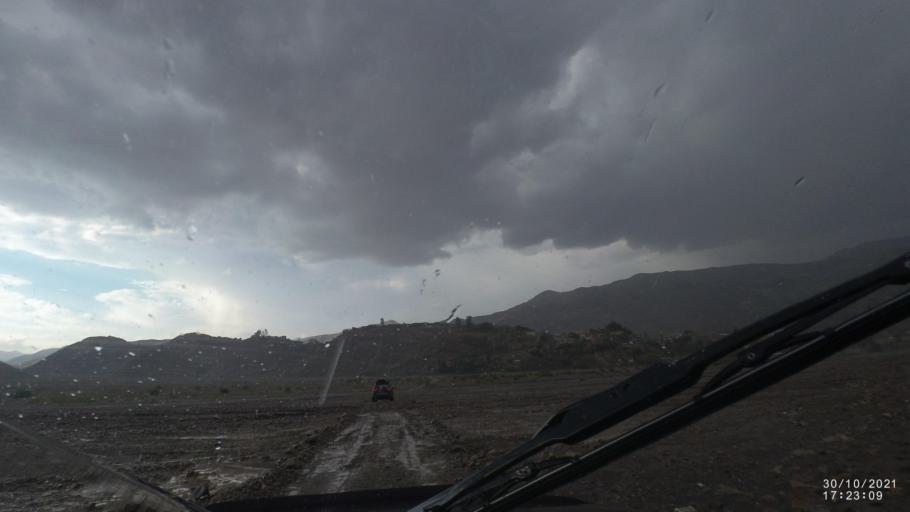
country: BO
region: Cochabamba
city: Colchani
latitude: -17.5213
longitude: -66.6221
